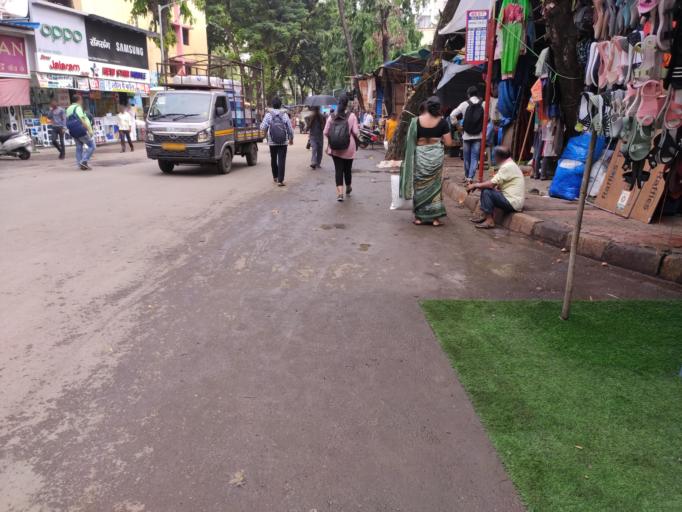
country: IN
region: Maharashtra
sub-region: Mumbai Suburban
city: Borivli
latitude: 19.2497
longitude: 72.8606
